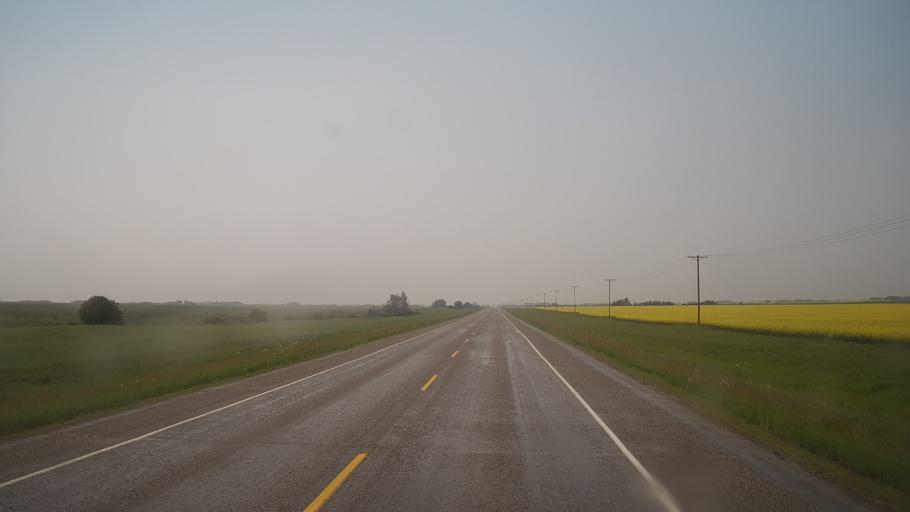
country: CA
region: Saskatchewan
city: Biggar
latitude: 52.1483
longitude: -108.2207
